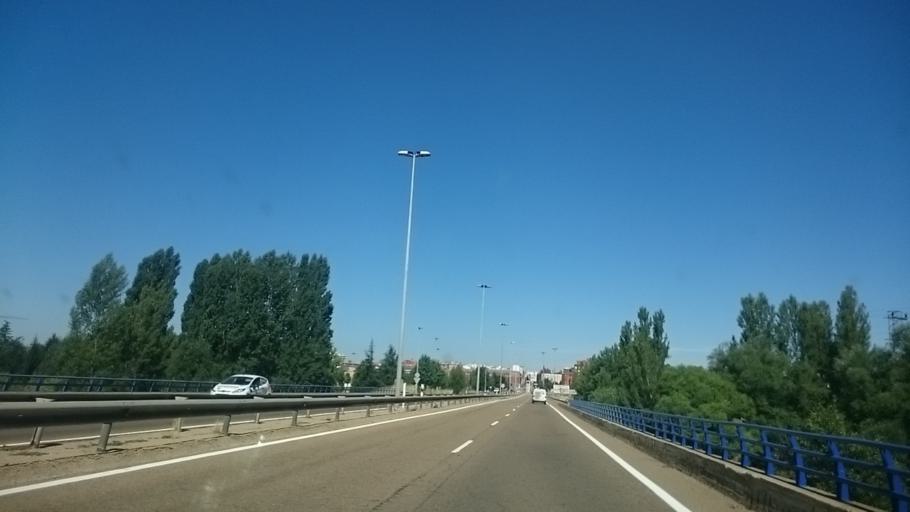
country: ES
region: Castille and Leon
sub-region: Provincia de Leon
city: Leon
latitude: 42.5857
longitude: -5.5510
